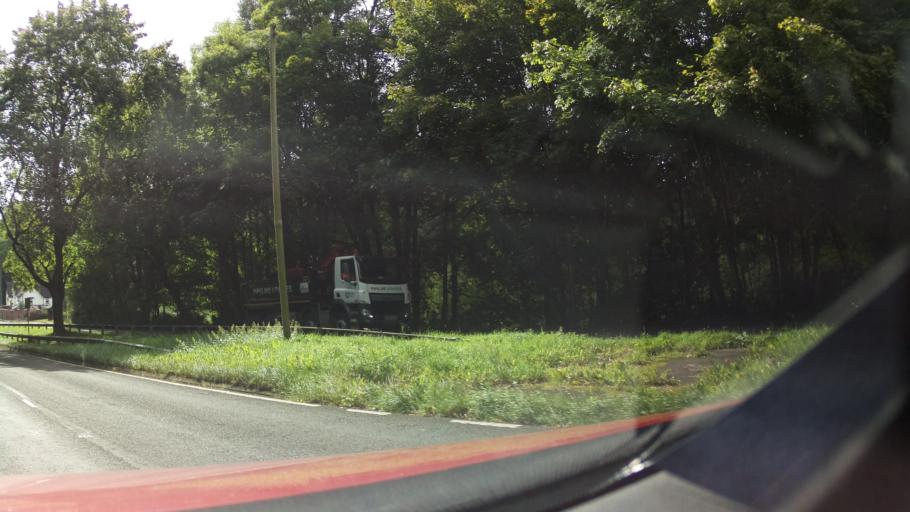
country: GB
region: England
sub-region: Staffordshire
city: Barlaston
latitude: 52.9396
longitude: -2.1879
